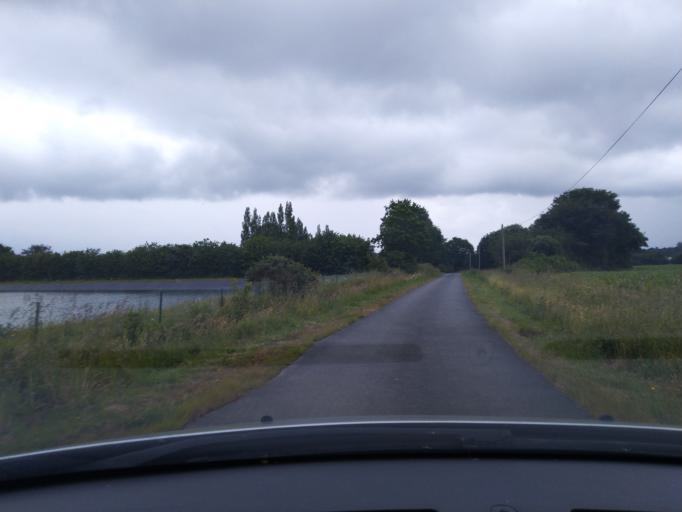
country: FR
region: Brittany
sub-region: Departement des Cotes-d'Armor
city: Begard
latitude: 48.6388
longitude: -3.3285
